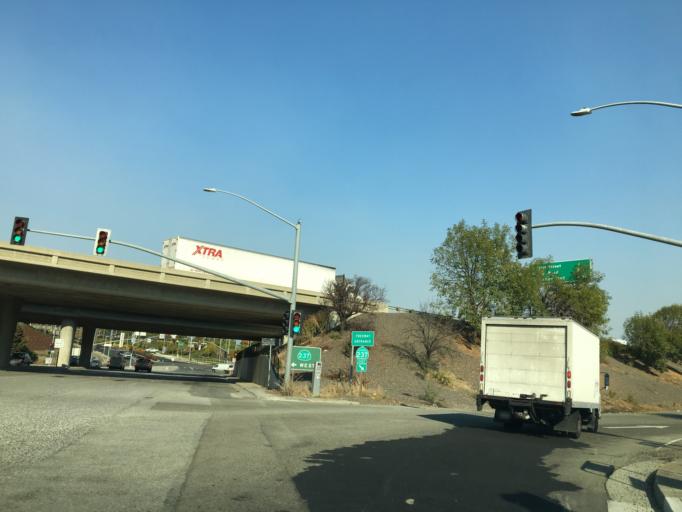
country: US
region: California
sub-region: Santa Clara County
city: Santa Clara
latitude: 37.4153
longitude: -121.9774
